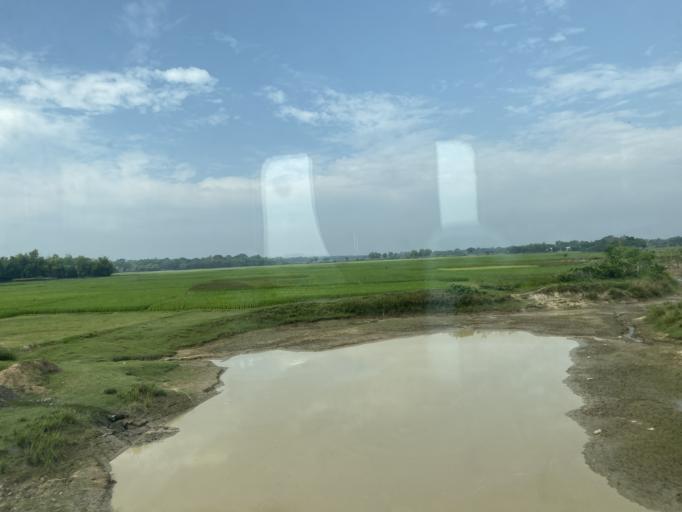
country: IN
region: Tripura
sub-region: West Tripura
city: Agartala
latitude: 23.9908
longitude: 91.2852
